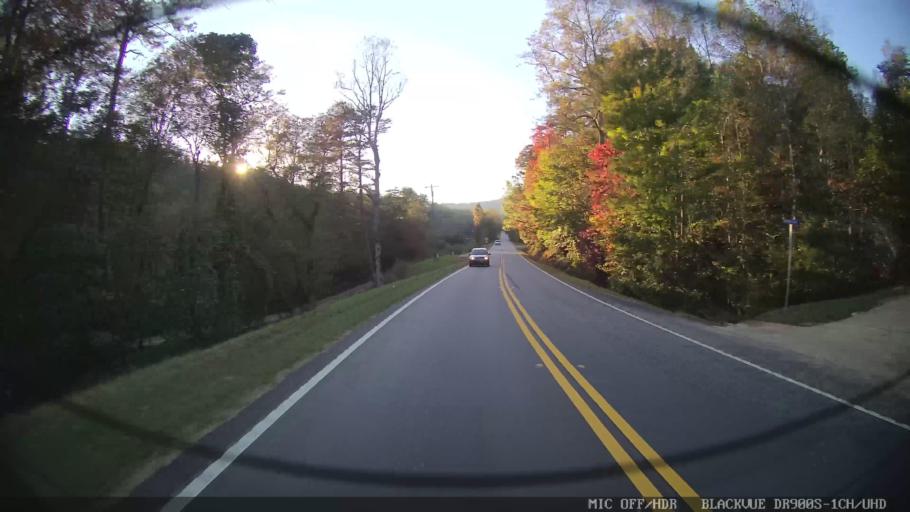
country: US
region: Georgia
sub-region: Lumpkin County
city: Dahlonega
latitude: 34.6321
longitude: -83.9195
